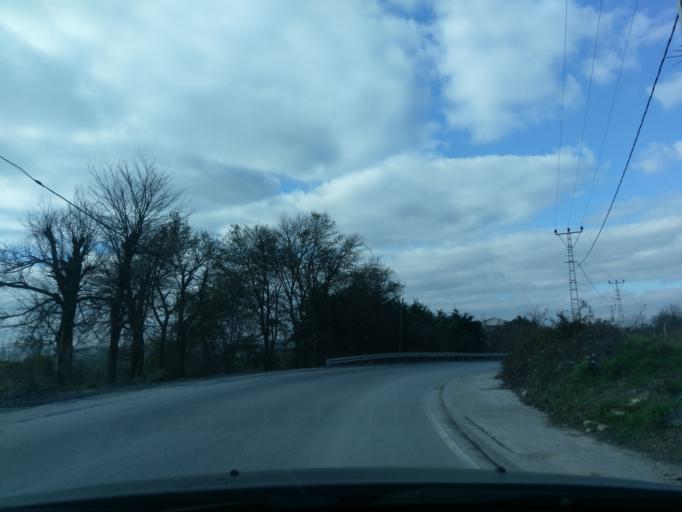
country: TR
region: Istanbul
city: Durusu
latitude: 41.2626
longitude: 28.6791
